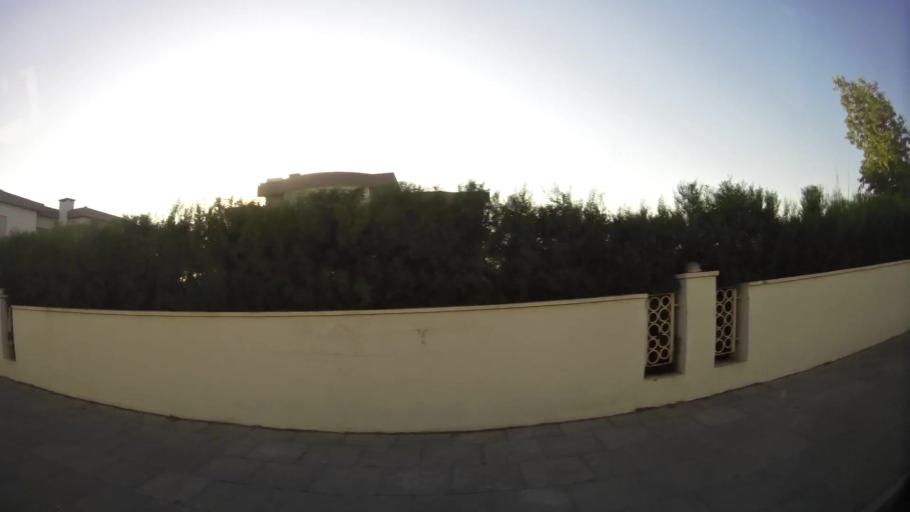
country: CY
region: Lefkosia
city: Nicosia
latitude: 35.1981
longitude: 33.3181
